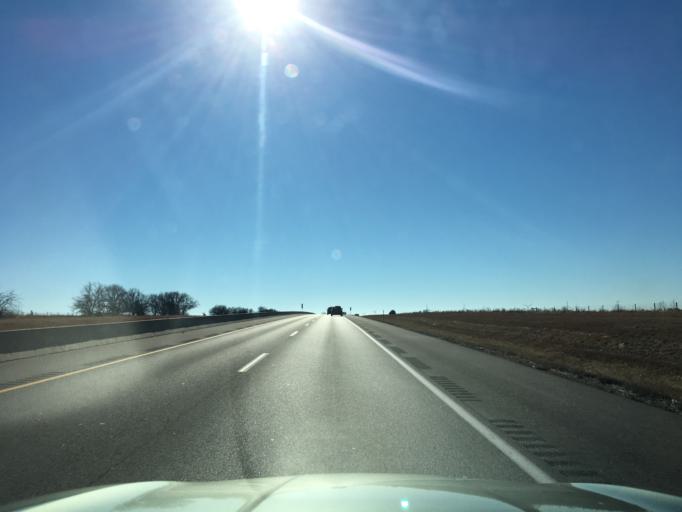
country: US
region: Kansas
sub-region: Sumner County
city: Wellington
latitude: 37.2029
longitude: -97.3402
